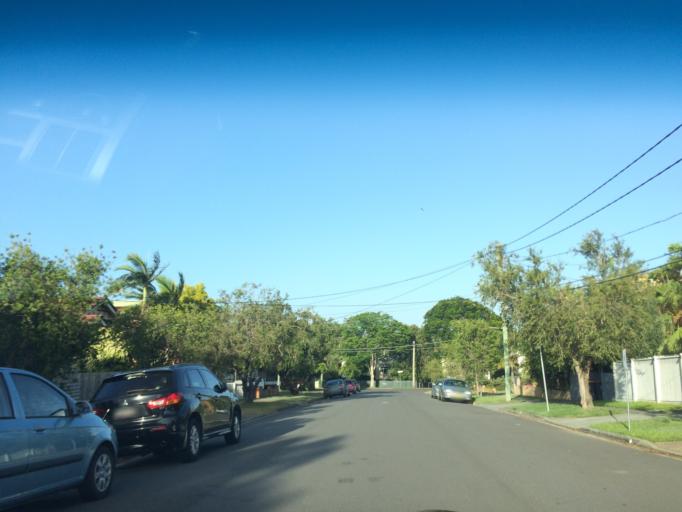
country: AU
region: Queensland
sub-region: Brisbane
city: Camp Hill
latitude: -27.4910
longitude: 153.0617
